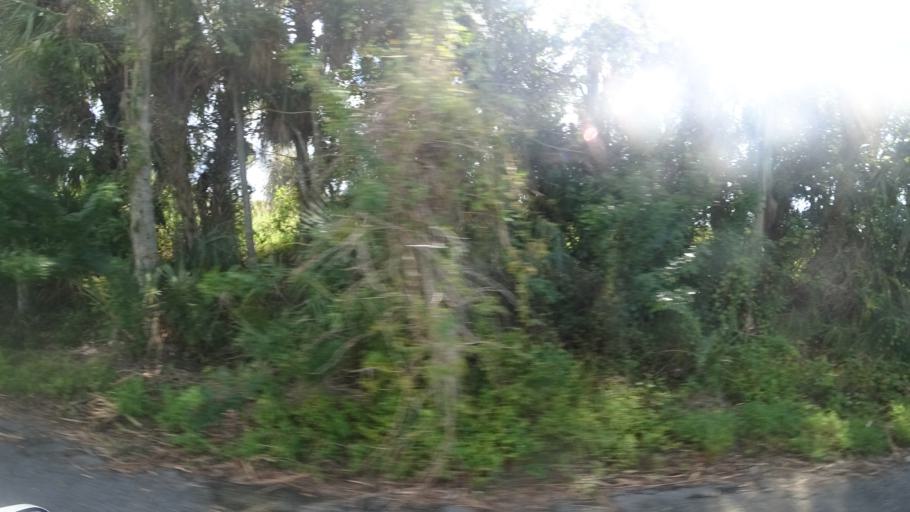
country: US
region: Florida
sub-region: Manatee County
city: Memphis
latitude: 27.5433
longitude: -82.5754
